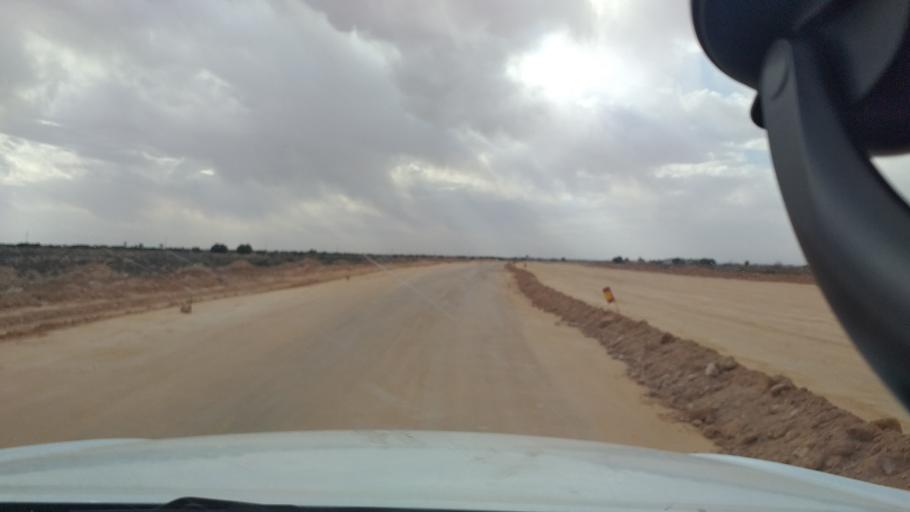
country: TN
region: Madanin
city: Medenine
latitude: 33.3085
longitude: 10.6136
